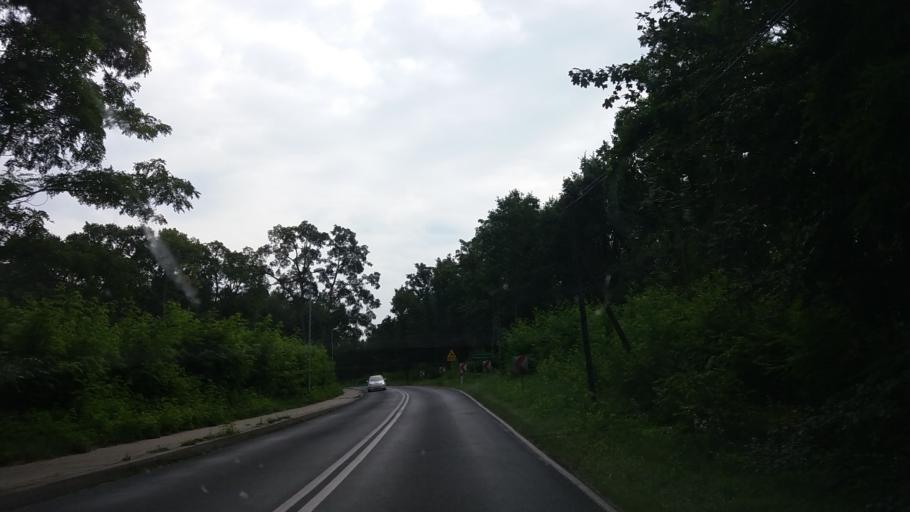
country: PL
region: Lubusz
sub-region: Powiat miedzyrzecki
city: Skwierzyna
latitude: 52.6398
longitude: 15.4529
